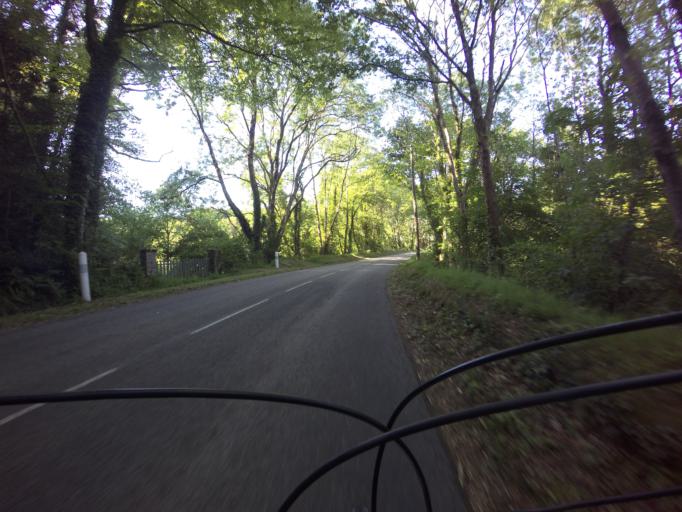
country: FR
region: Brittany
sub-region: Departement du Finistere
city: Quimper
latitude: 48.0180
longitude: -4.1357
